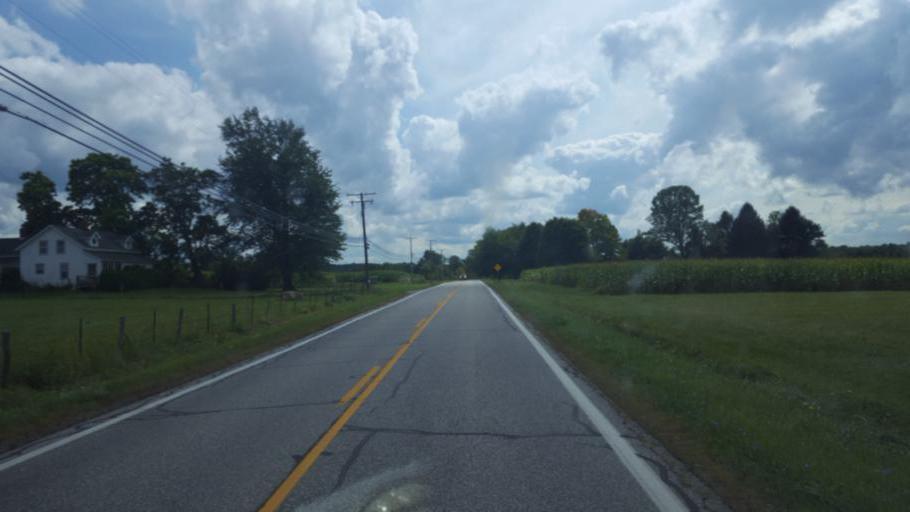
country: US
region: Ohio
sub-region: Geauga County
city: Burton
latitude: 41.4071
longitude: -81.1450
